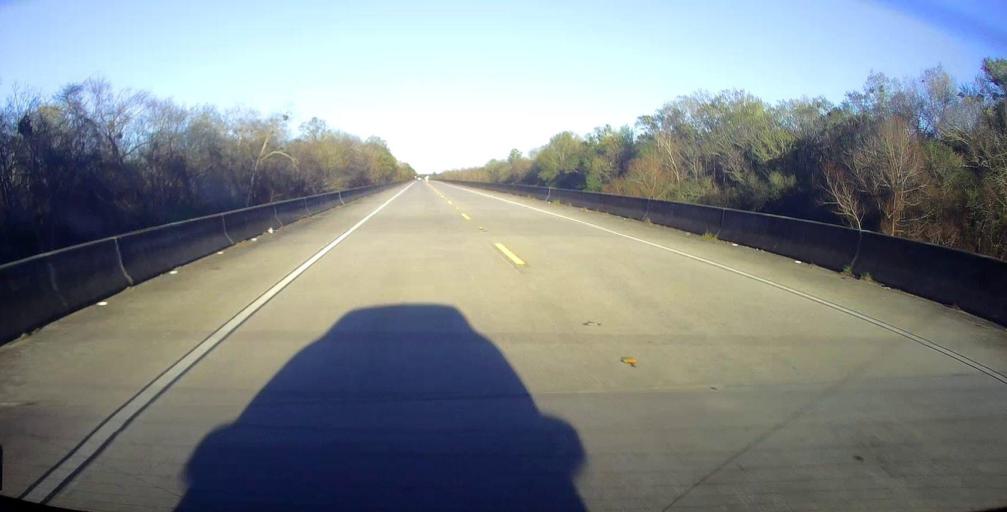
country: US
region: Georgia
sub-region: Wilcox County
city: Abbeville
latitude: 31.9957
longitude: -83.2850
